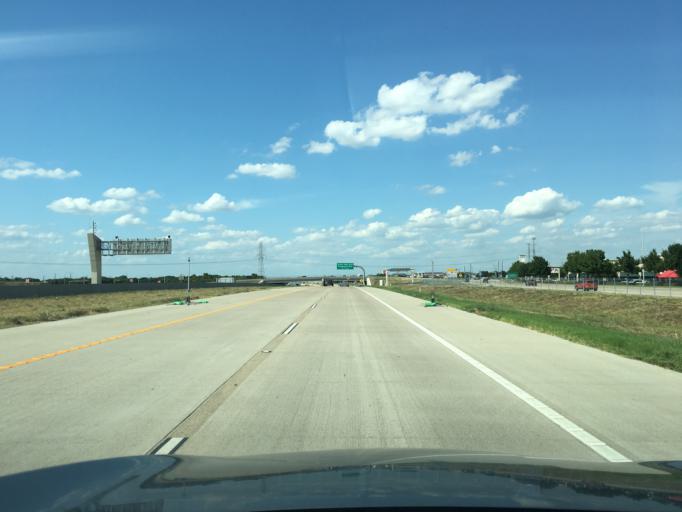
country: US
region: Texas
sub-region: Tarrant County
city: Arlington
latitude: 32.6442
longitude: -97.0626
